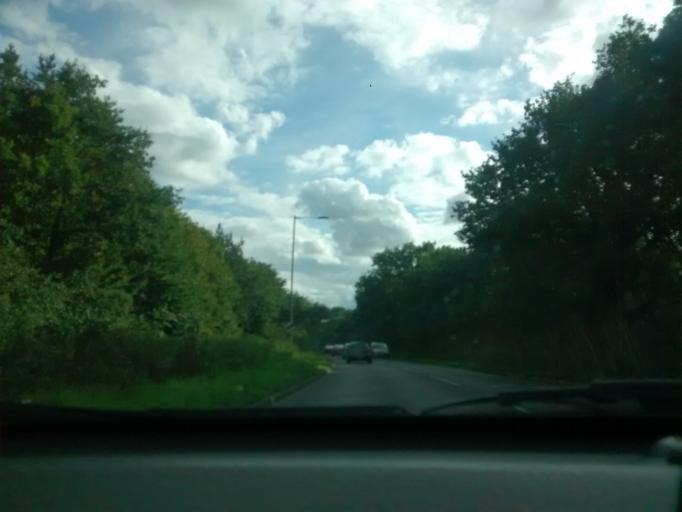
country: GB
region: England
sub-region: Norfolk
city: King's Lynn
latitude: 52.6827
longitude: 0.4216
